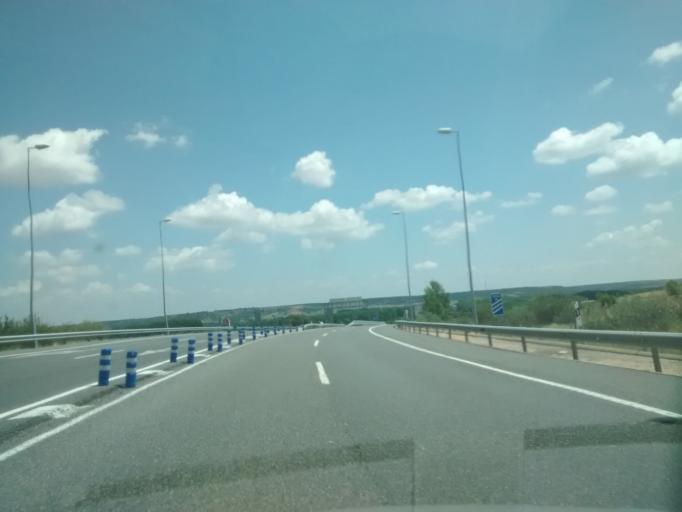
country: ES
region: Castille and Leon
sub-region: Provincia de Leon
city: Astorga
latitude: 42.4384
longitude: -6.0458
